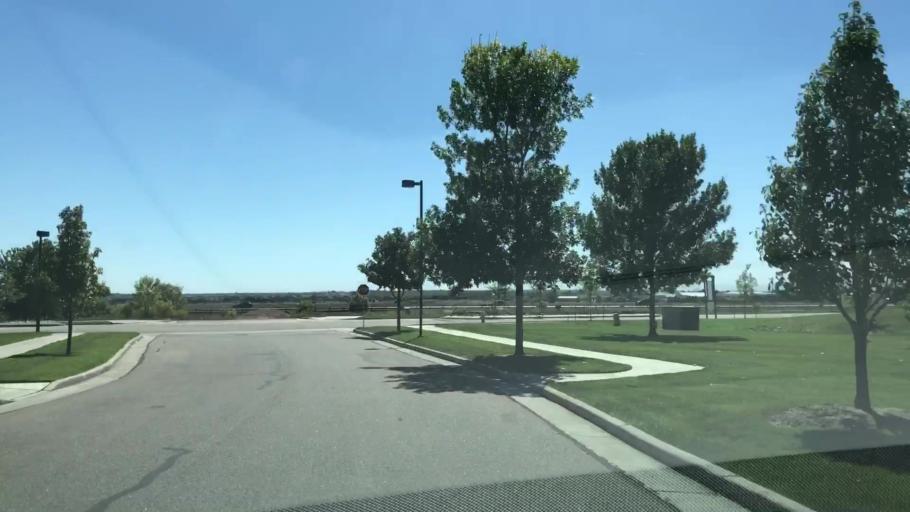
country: US
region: Colorado
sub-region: Weld County
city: Windsor
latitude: 40.5247
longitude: -104.9569
